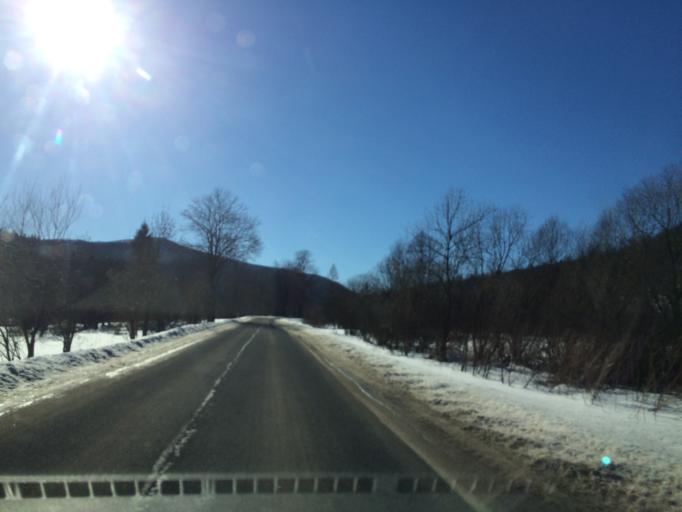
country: PL
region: Subcarpathian Voivodeship
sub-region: Powiat bieszczadzki
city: Lutowiska
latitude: 49.1340
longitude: 22.6693
